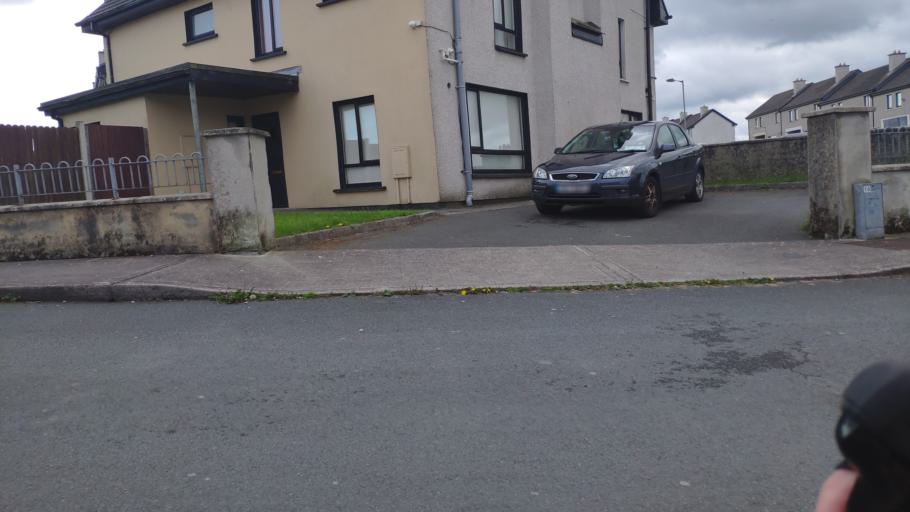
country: IE
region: Munster
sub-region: County Cork
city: Cork
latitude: 51.9130
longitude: -8.5003
